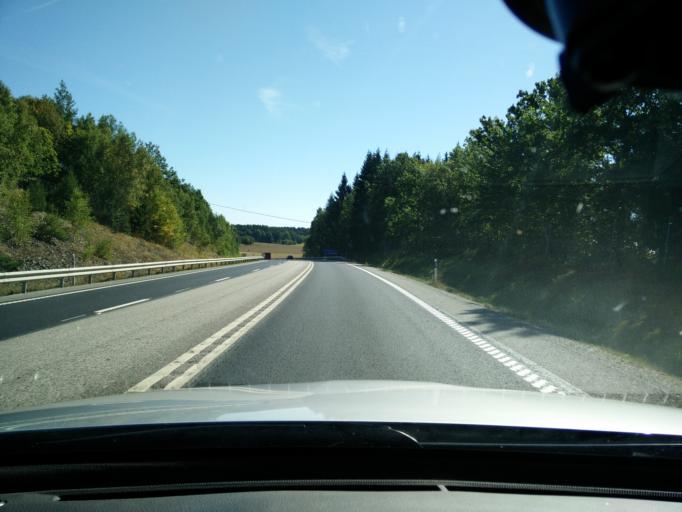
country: SE
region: Stockholm
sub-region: Lidingo
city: Lidingoe
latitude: 59.4528
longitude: 18.1833
